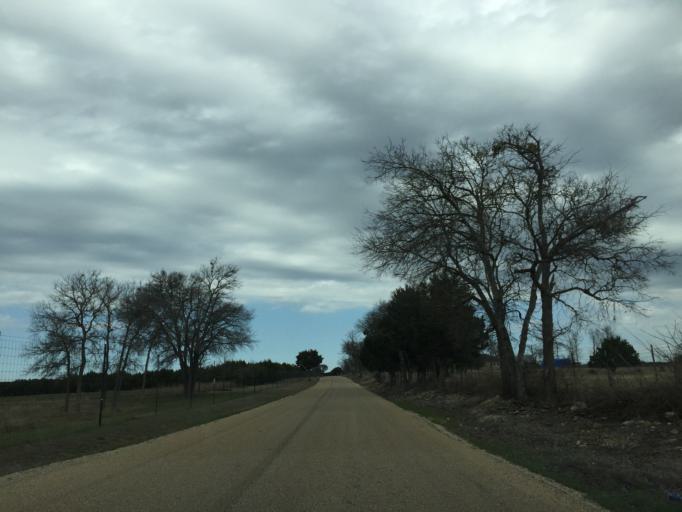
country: US
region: Texas
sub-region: Burnet County
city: Bertram
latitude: 30.6477
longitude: -98.0137
